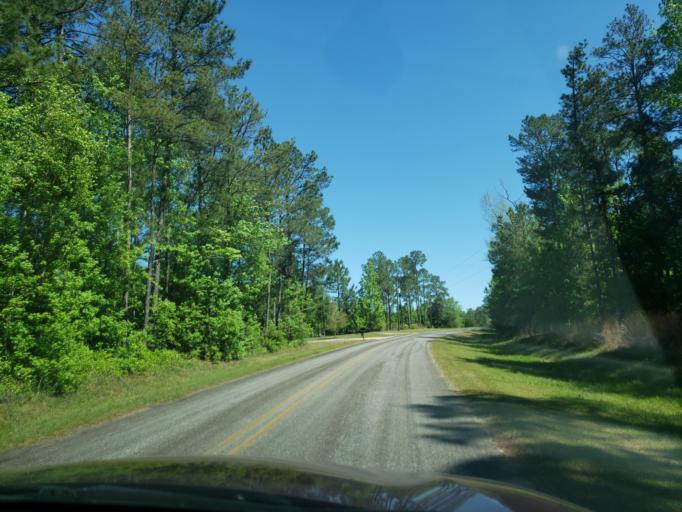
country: US
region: Alabama
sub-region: Elmore County
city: Eclectic
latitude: 32.7003
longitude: -85.8881
